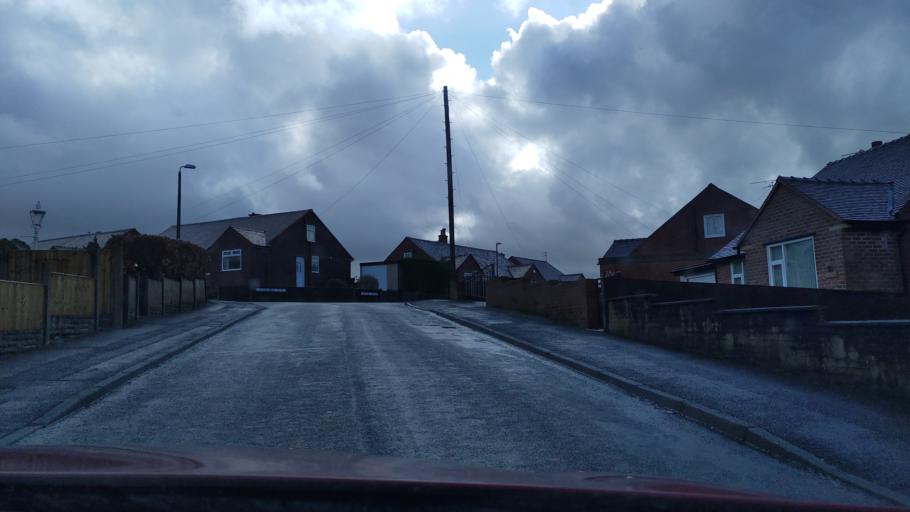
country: GB
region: England
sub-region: Lancashire
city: Chorley
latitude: 53.6482
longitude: -2.6219
